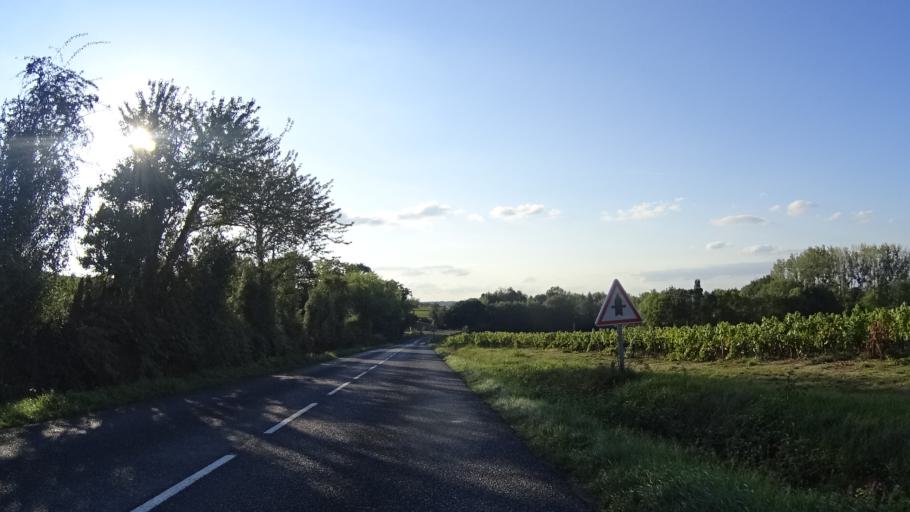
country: FR
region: Pays de la Loire
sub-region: Departement de Maine-et-Loire
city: Lire
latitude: 47.3410
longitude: -1.1410
